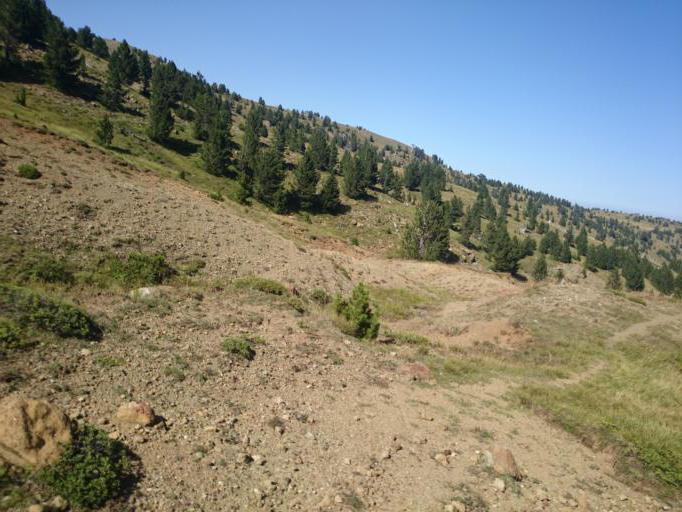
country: AL
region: Elbasan
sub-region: Rrethi i Gramshit
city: Lenias
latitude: 40.8233
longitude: 20.4591
